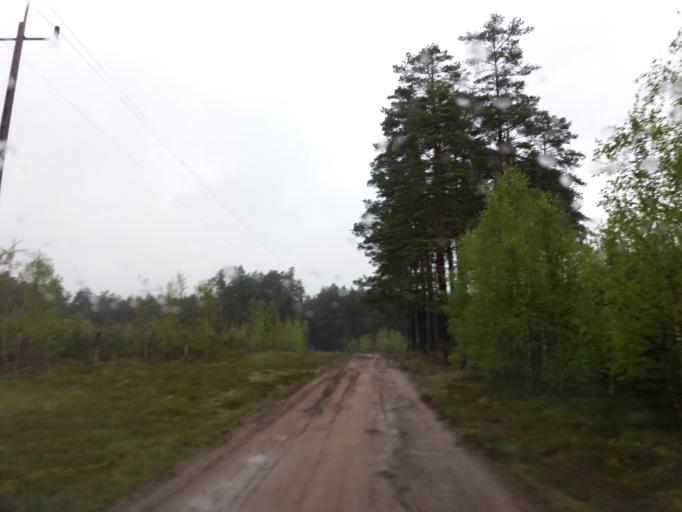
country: PL
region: West Pomeranian Voivodeship
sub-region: Powiat drawski
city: Kalisz Pomorski
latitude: 53.1642
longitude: 15.9815
